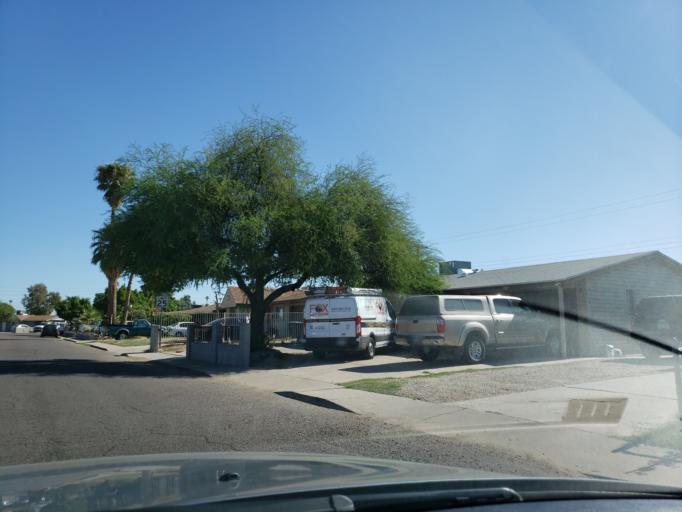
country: US
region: Arizona
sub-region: Maricopa County
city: Glendale
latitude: 33.4774
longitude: -112.1626
